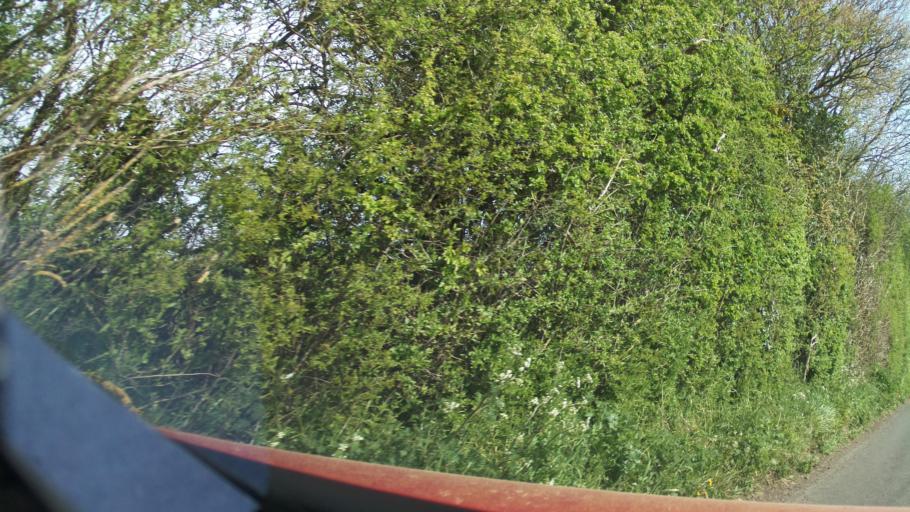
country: GB
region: England
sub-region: Somerset
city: Ilchester
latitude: 51.0156
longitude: -2.6076
